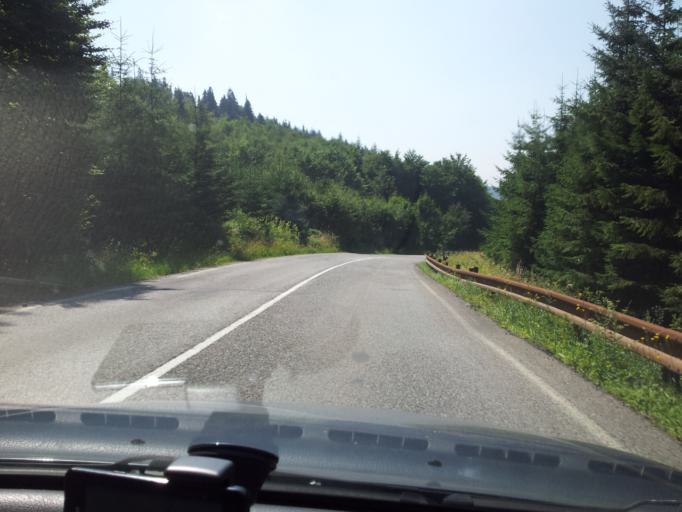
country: SK
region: Zilinsky
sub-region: Okres Dolny Kubin
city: Dolny Kubin
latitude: 49.2995
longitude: 19.3530
